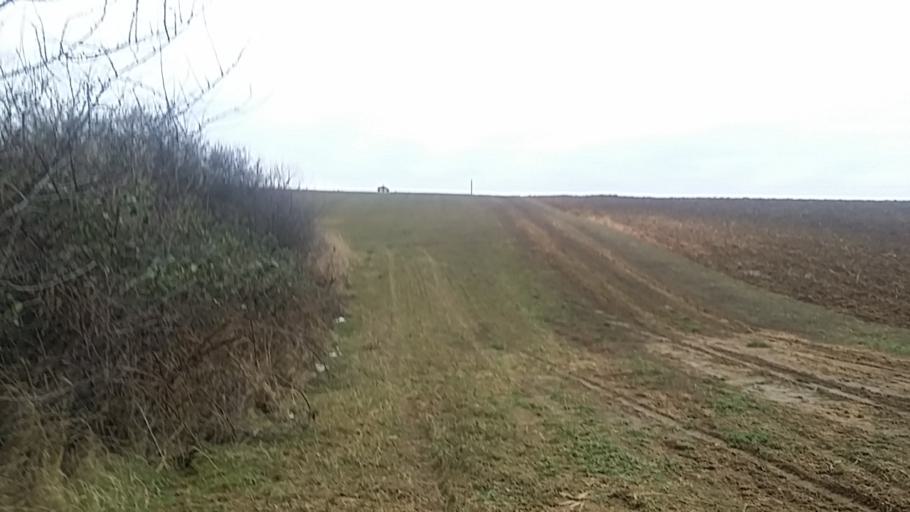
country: HU
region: Baranya
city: Pecsvarad
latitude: 46.1242
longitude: 18.5271
